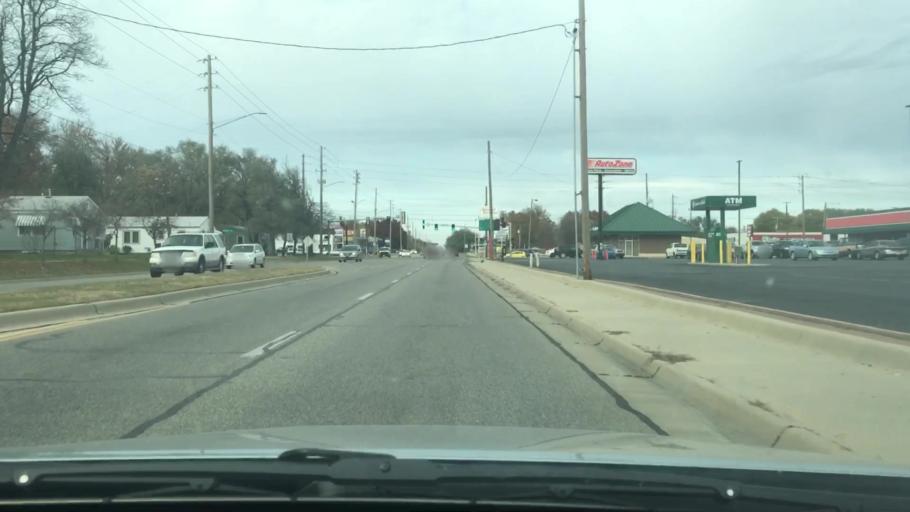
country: US
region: Kansas
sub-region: Sedgwick County
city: Wichita
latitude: 37.6705
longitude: -97.2804
